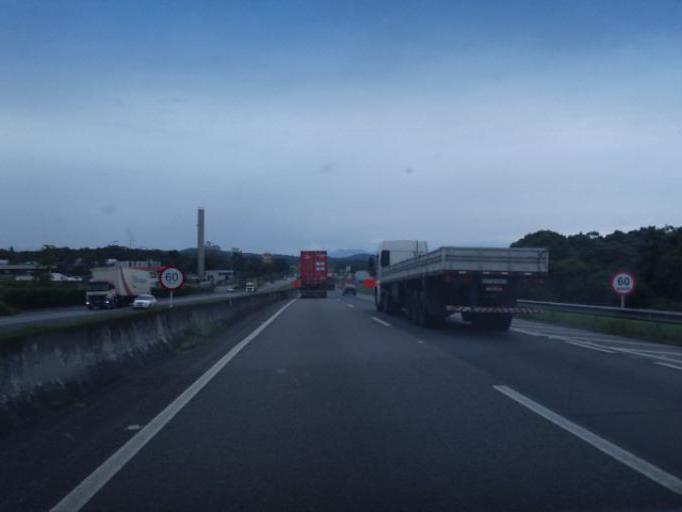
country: BR
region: Sao Paulo
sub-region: Pariquera-Acu
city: Pariquera Acu
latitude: -24.6206
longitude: -47.8937
